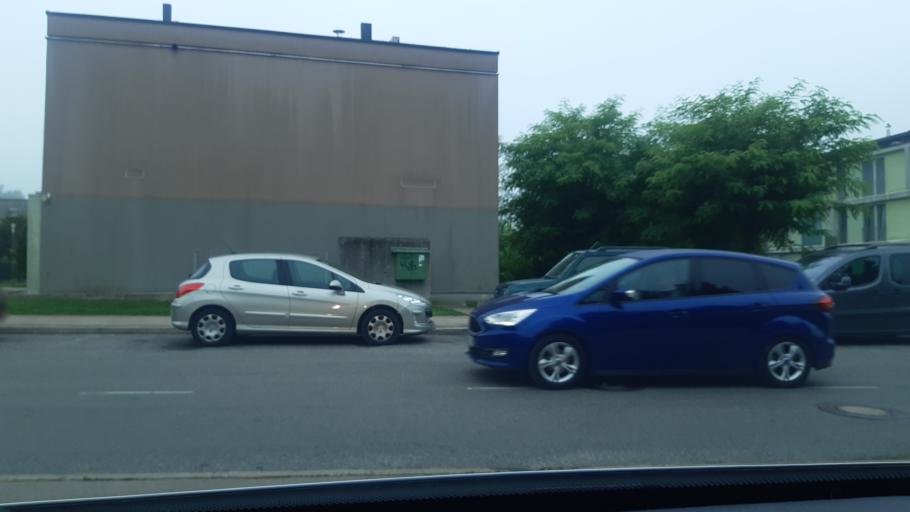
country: SI
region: Ljubljana
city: Ljubljana
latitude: 46.0682
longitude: 14.4734
